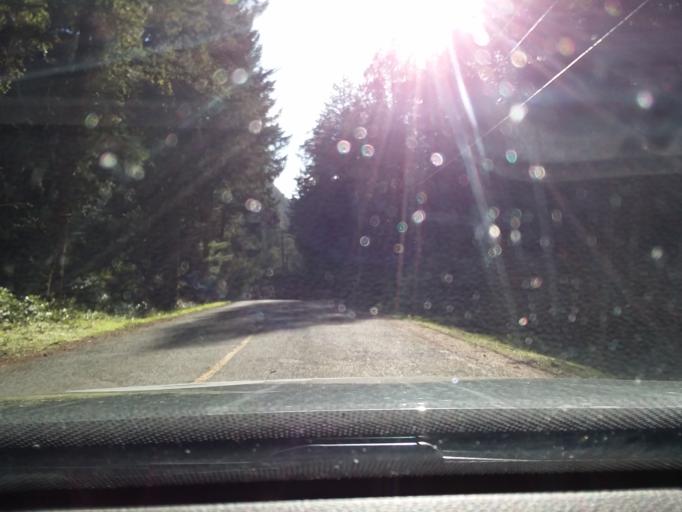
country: CA
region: British Columbia
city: North Cowichan
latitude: 48.9346
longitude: -123.4794
